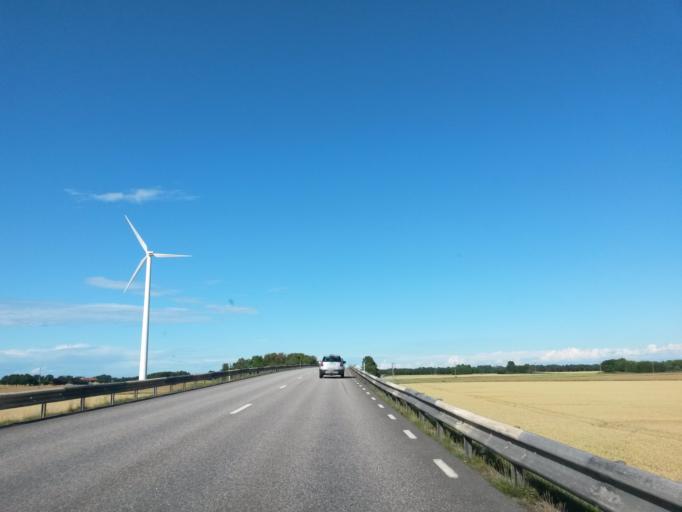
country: SE
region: Vaestra Goetaland
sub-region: Grastorps Kommun
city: Graestorp
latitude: 58.3413
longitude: 12.6251
